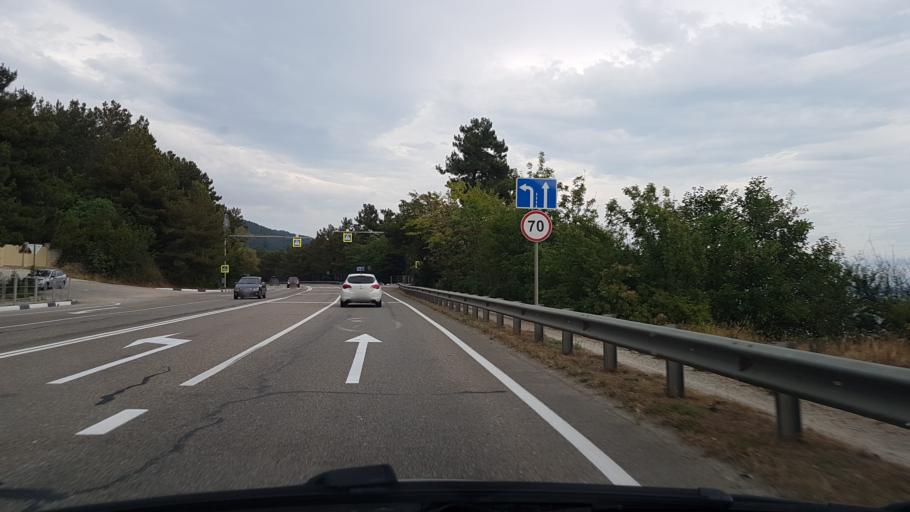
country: RU
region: Krasnodarskiy
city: Ol'ginka
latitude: 44.1864
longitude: 38.9011
